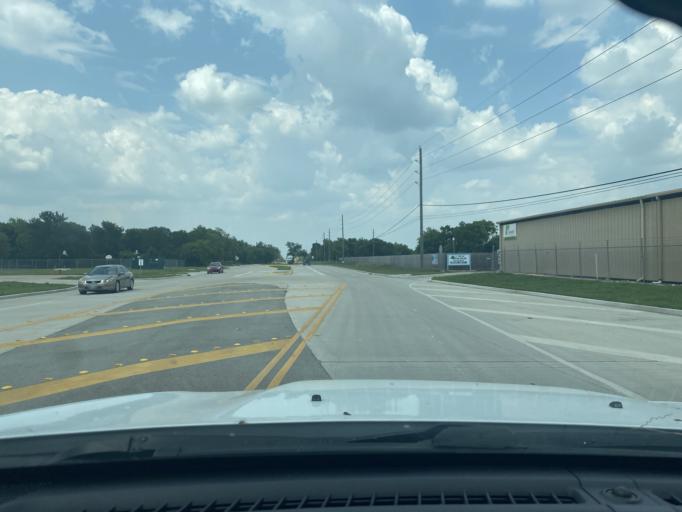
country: US
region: Texas
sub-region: Fort Bend County
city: Greatwood
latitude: 29.5410
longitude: -95.7246
